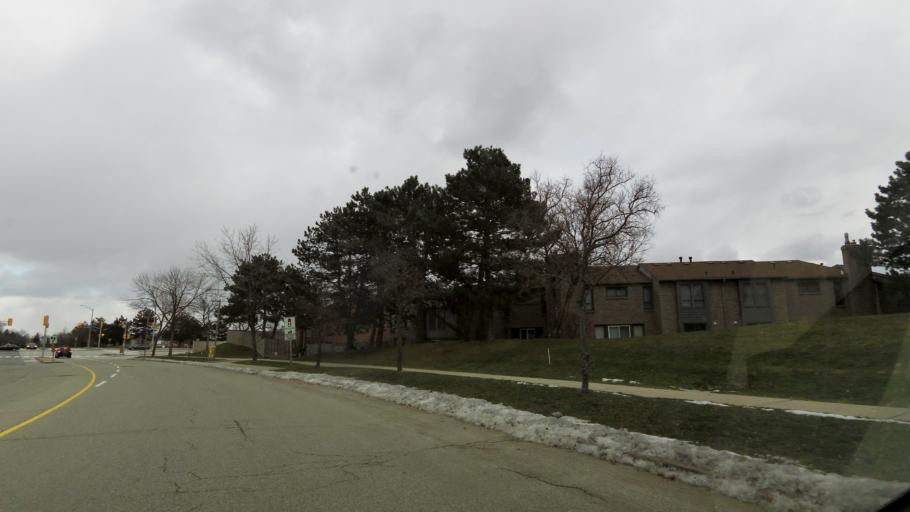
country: CA
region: Ontario
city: Mississauga
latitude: 43.5499
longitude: -79.6908
